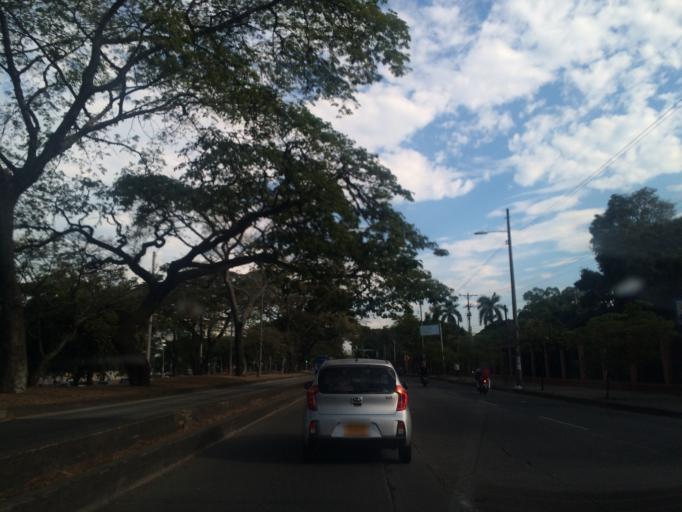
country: CO
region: Valle del Cauca
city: Cali
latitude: 3.3845
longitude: -76.5446
